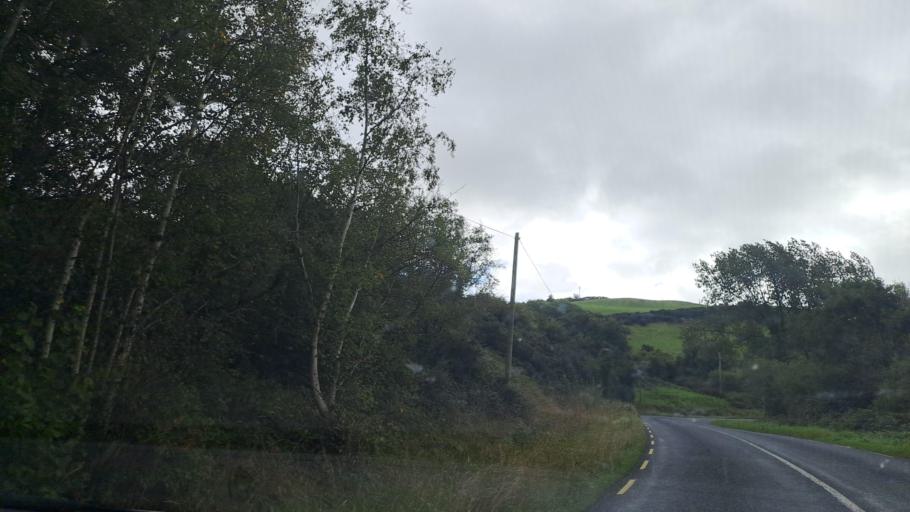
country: IE
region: Ulster
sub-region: An Cabhan
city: Bailieborough
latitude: 53.9674
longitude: -6.9157
